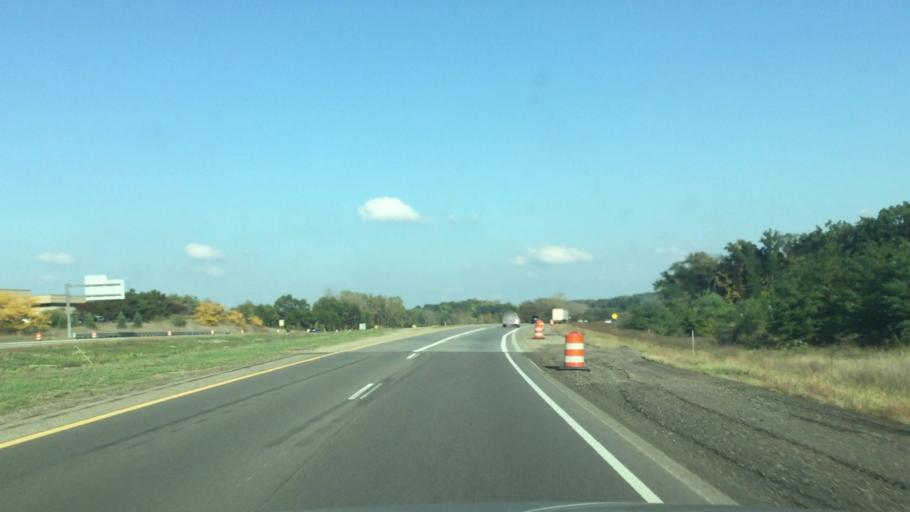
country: US
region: Michigan
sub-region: Jackson County
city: Michigan Center
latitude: 42.2804
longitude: -84.3065
